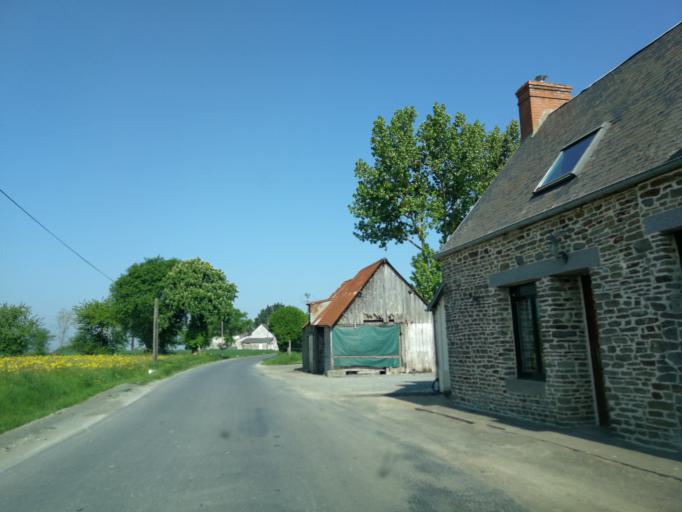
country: FR
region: Lower Normandy
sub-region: Departement de la Manche
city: Pontorson
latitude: 48.5677
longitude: -1.4328
